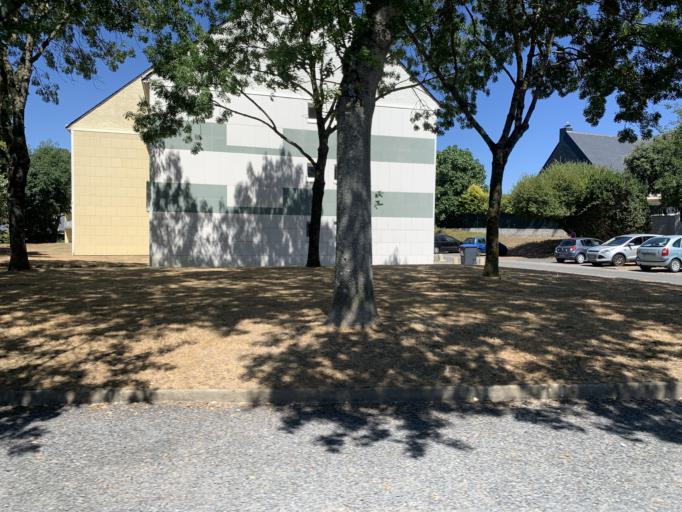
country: FR
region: Pays de la Loire
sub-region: Departement de la Loire-Atlantique
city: Pornichet
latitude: 47.2535
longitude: -2.3154
